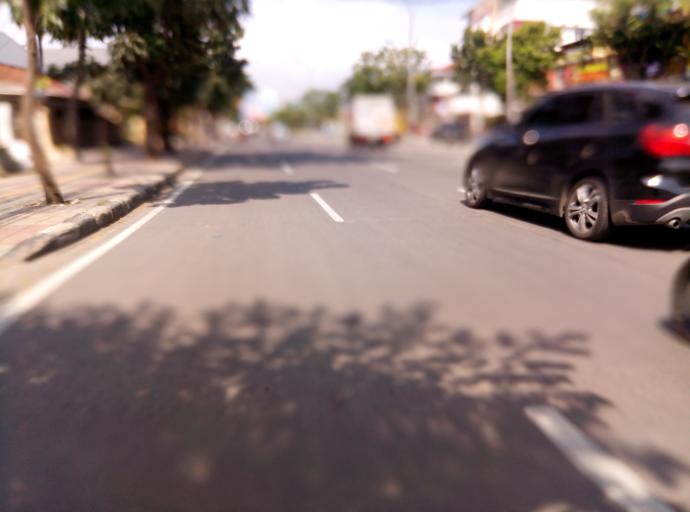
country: ID
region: West Java
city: Bandung
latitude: -6.9416
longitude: 107.6423
